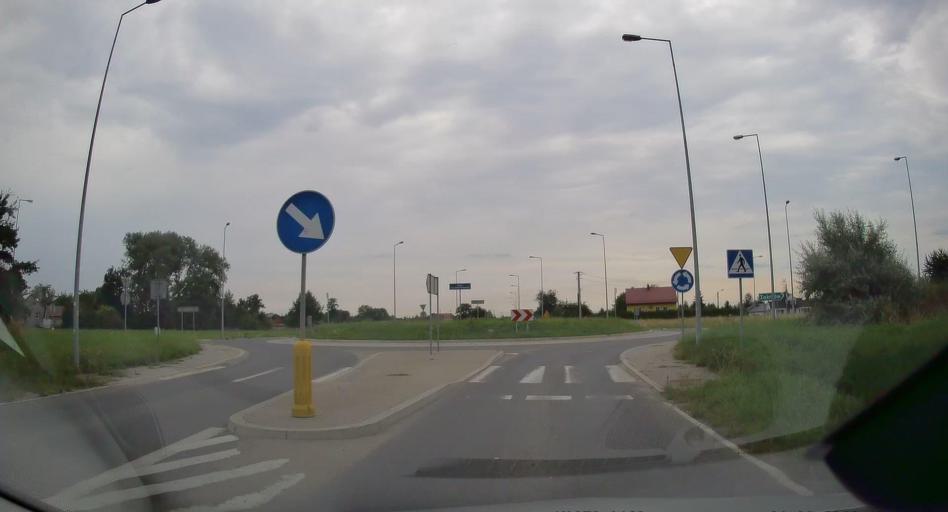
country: PL
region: Lesser Poland Voivodeship
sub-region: Powiat tarnowski
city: Wojnicz
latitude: 49.9737
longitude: 20.8439
